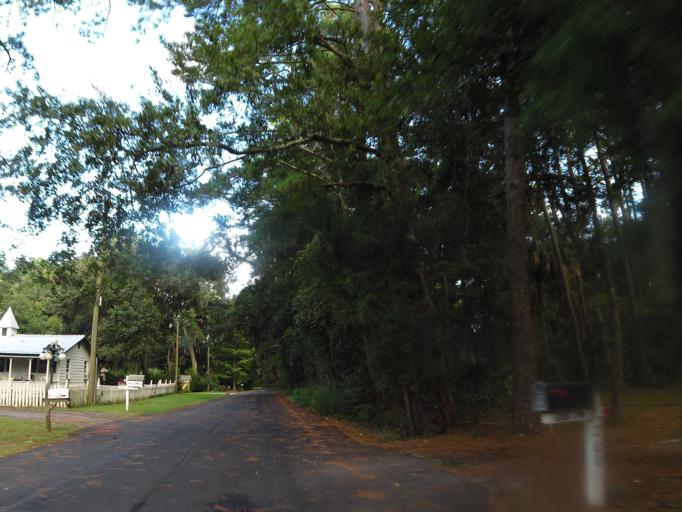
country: US
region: Georgia
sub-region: Glynn County
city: Country Club Estates
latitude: 31.2567
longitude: -81.4372
